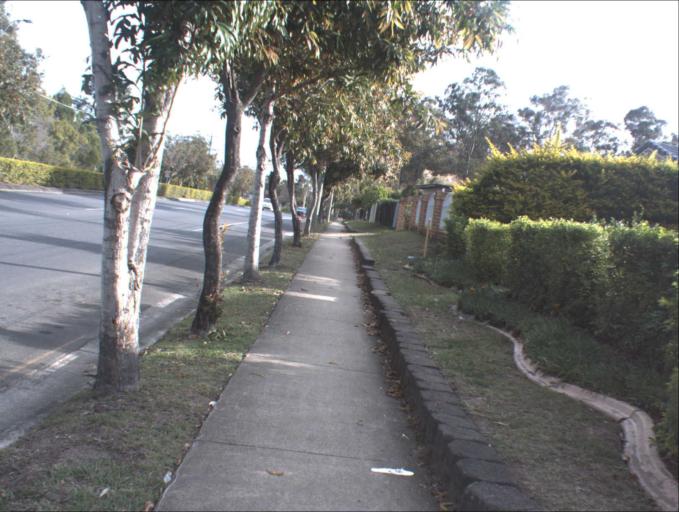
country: AU
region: Queensland
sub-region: Logan
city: Waterford West
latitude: -27.6894
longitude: 153.1043
